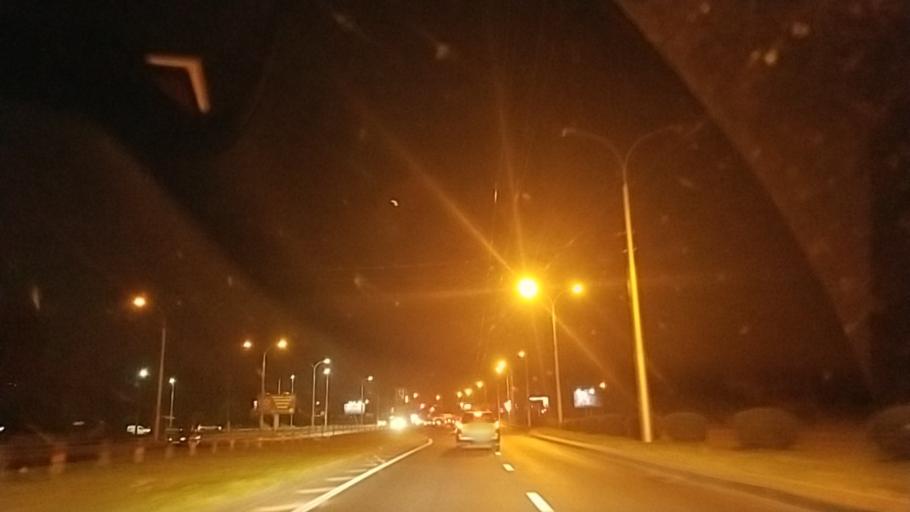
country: BY
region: Brest
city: Brest
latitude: 52.0822
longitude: 23.7713
